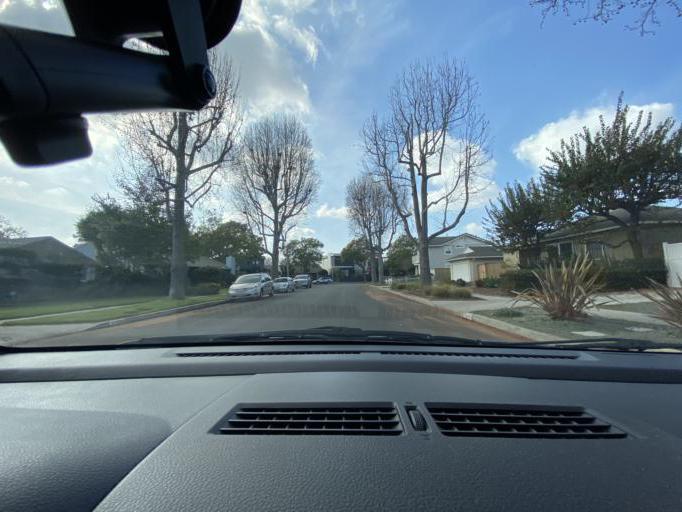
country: US
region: California
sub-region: Los Angeles County
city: Culver City
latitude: 34.0183
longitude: -118.4304
